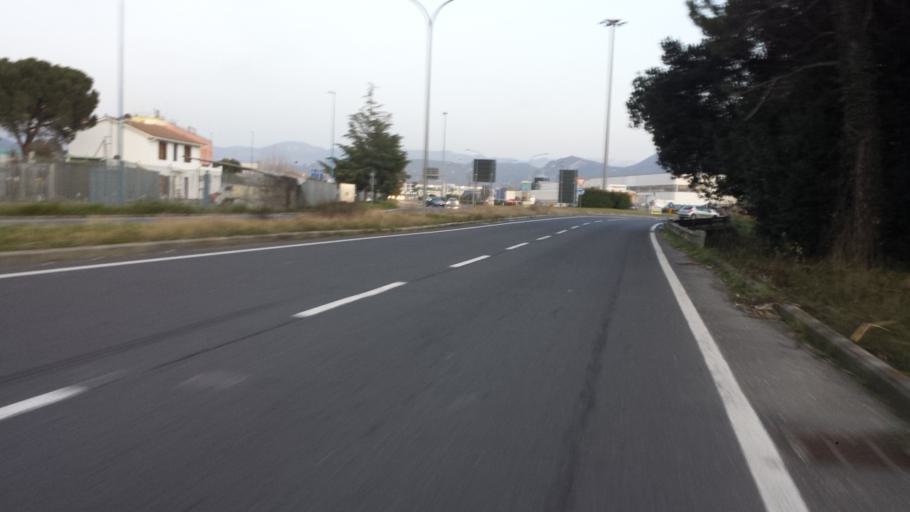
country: IT
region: Umbria
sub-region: Provincia di Terni
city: Terni
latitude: 42.5670
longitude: 12.6045
